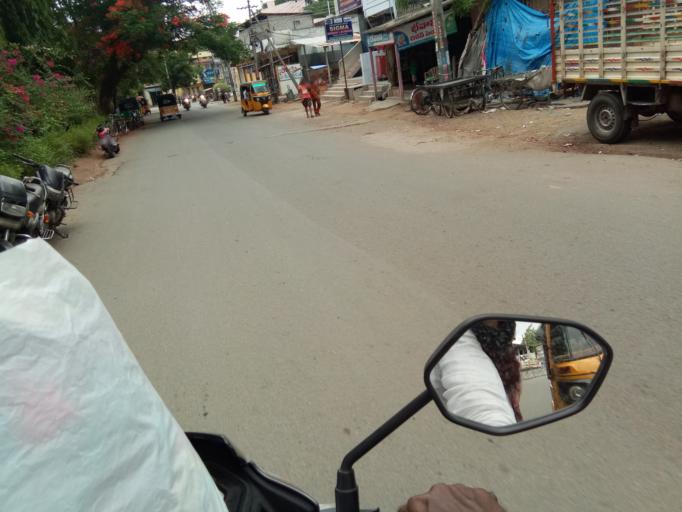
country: IN
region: Telangana
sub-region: Khammam
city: Khammam
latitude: 17.2406
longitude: 80.1426
